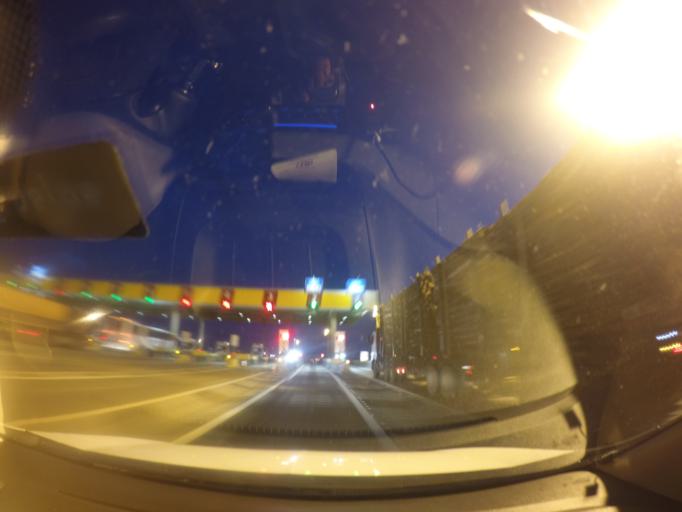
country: BR
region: Sao Paulo
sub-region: Limeira
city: Limeira
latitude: -22.5098
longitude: -47.3980
